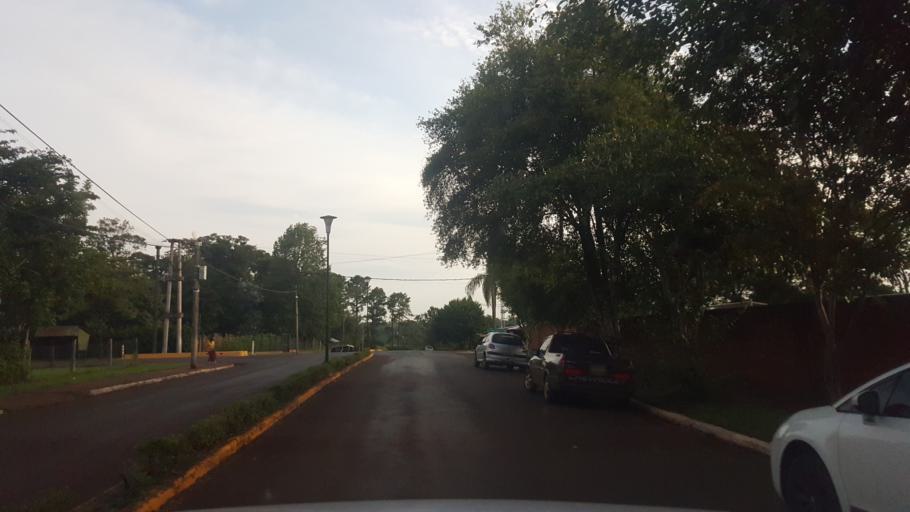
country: AR
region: Misiones
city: Capiovi
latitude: -26.9342
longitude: -55.0578
